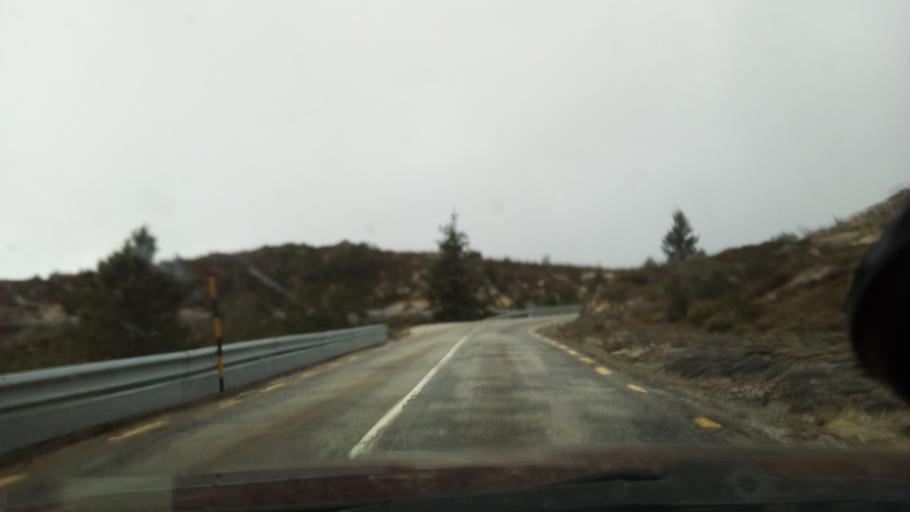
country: PT
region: Guarda
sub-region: Manteigas
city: Manteigas
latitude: 40.4161
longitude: -7.5528
